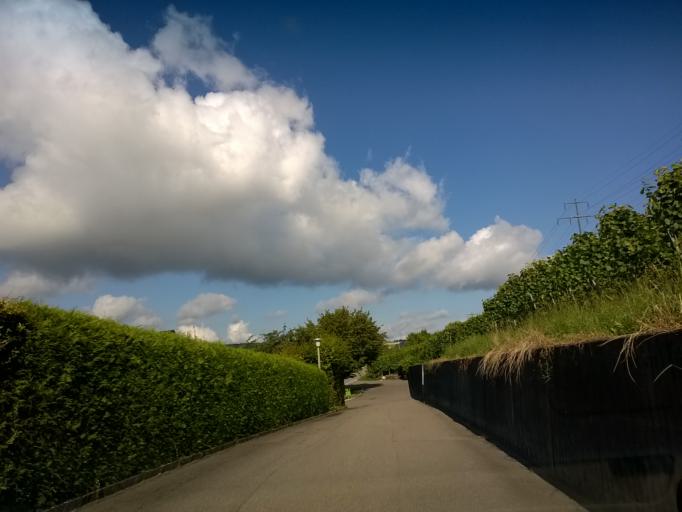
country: CH
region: Zurich
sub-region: Bezirk Buelach
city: Embrach / Embrach (Dorfkern)
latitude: 47.4907
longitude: 8.6141
